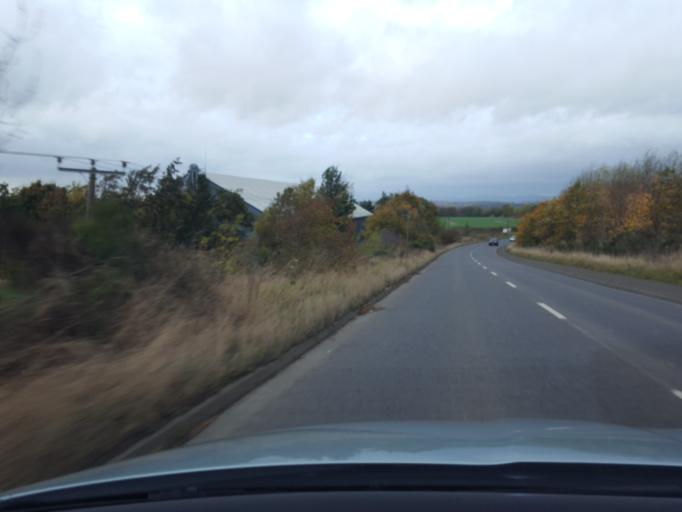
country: GB
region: Scotland
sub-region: Edinburgh
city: Newbridge
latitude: 55.9139
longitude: -3.4077
